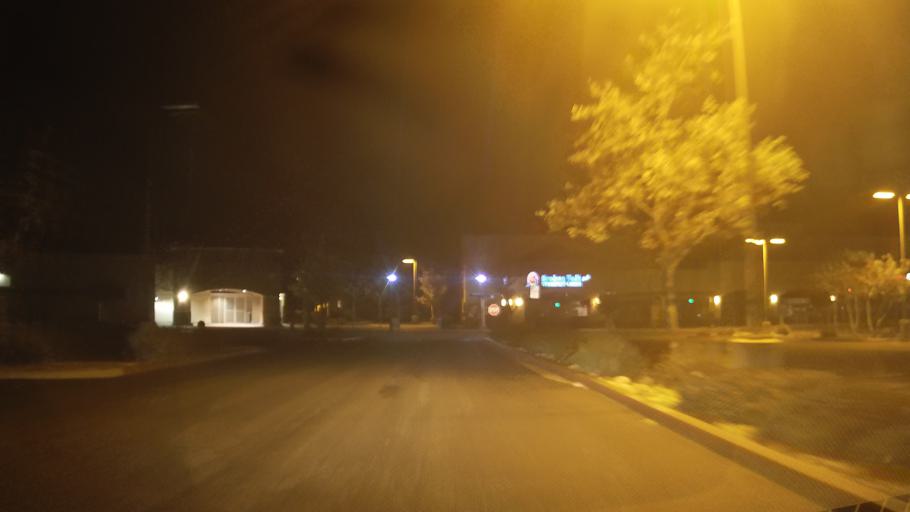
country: US
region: California
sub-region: San Diego County
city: Rancho San Diego
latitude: 32.7386
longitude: -116.9398
